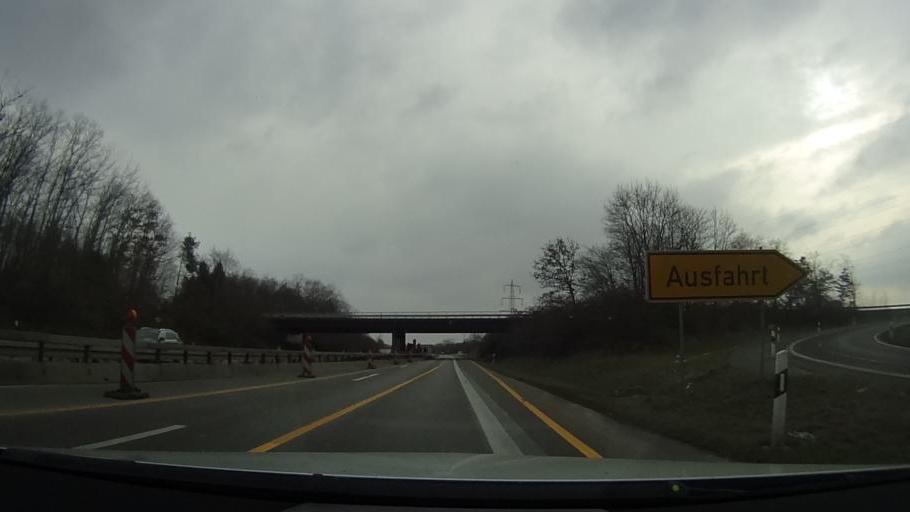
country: DE
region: Hesse
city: Kelsterbach
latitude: 50.0626
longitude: 8.5501
